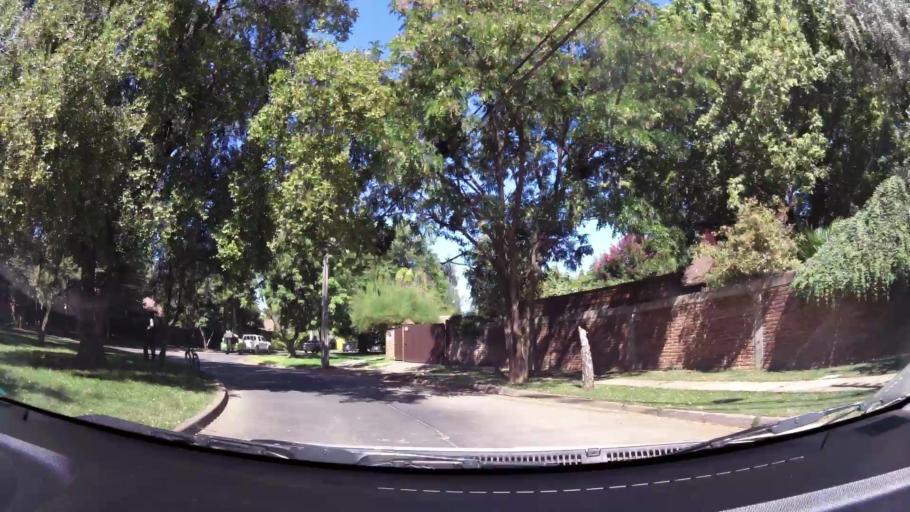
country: CL
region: Maule
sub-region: Provincia de Talca
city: Talca
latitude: -35.4307
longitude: -71.6190
